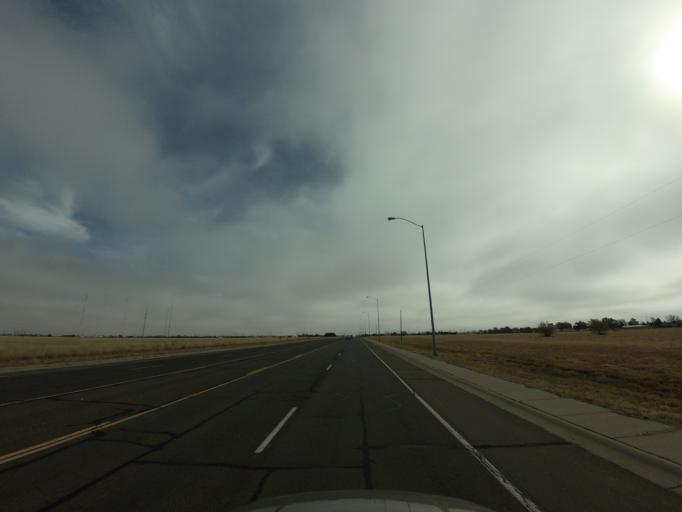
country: US
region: New Mexico
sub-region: Curry County
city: Clovis
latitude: 34.4340
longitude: -103.2203
